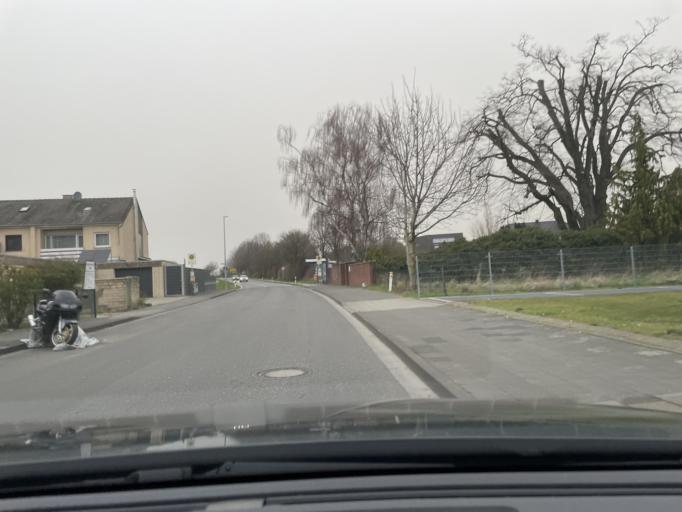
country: DE
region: North Rhine-Westphalia
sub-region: Regierungsbezirk Dusseldorf
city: Juchen
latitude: 51.1027
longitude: 6.4523
